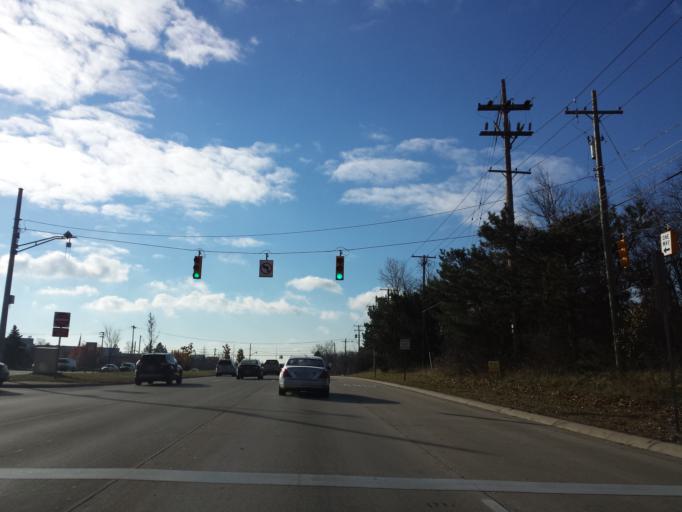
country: US
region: Michigan
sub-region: Oakland County
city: Bingham Farms
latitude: 42.5174
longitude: -83.2860
